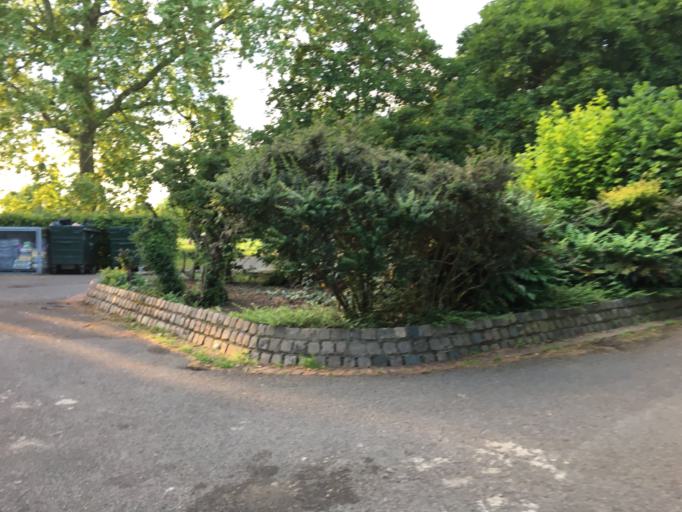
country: GB
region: England
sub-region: Greater London
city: Camden Town
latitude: 51.5311
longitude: -0.1503
